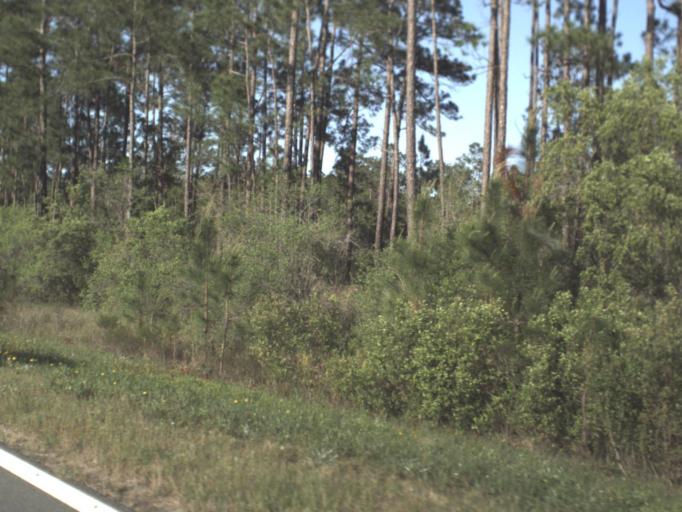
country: US
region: Florida
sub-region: Liberty County
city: Bristol
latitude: 30.2966
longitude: -84.8328
